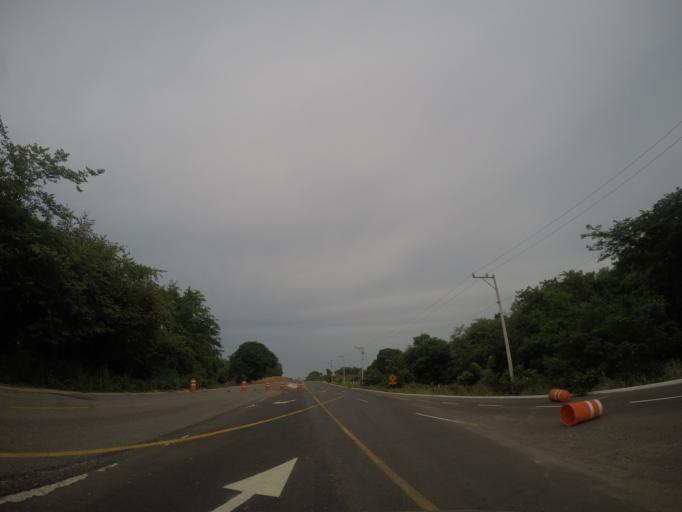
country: MX
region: Oaxaca
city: Santa Maria Tonameca
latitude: 15.7232
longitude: -96.6189
